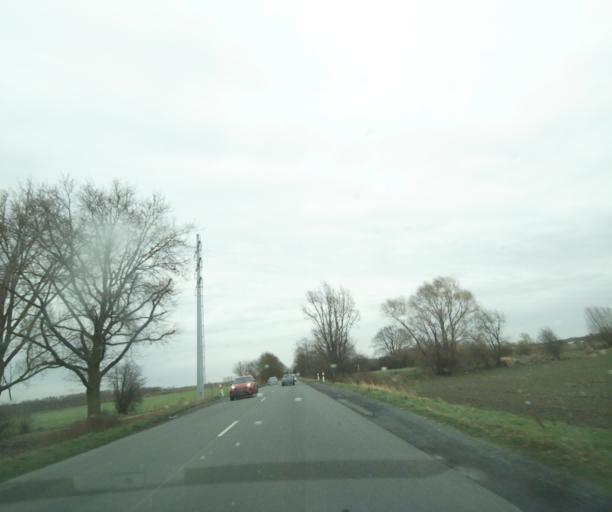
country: FR
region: Nord-Pas-de-Calais
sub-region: Departement du Nord
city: Quarouble
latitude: 50.4019
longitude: 3.6314
